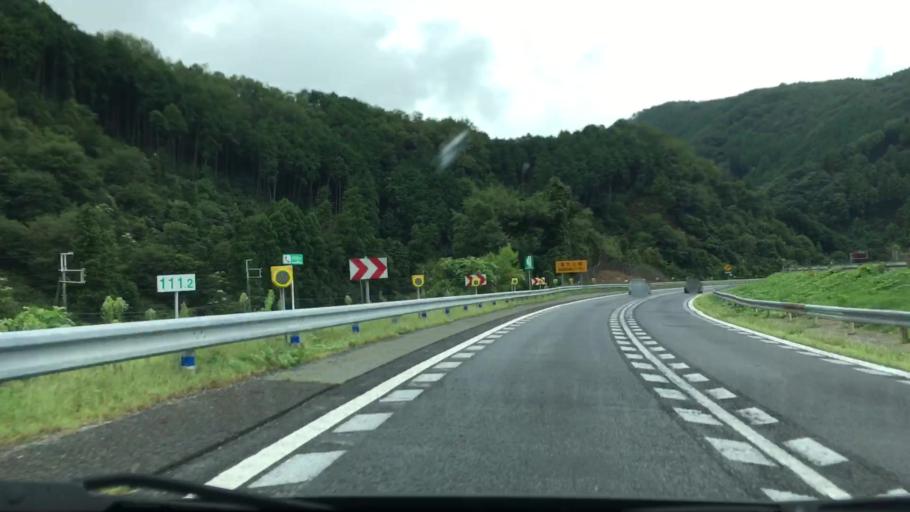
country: JP
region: Hyogo
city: Yamazakicho-nakabirose
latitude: 35.0417
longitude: 134.4476
